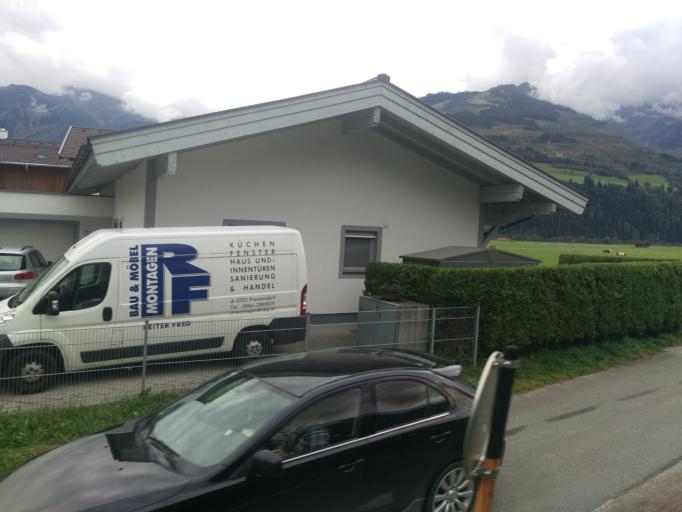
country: AT
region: Salzburg
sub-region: Politischer Bezirk Zell am See
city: Piesendorf
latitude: 47.2896
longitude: 12.7203
